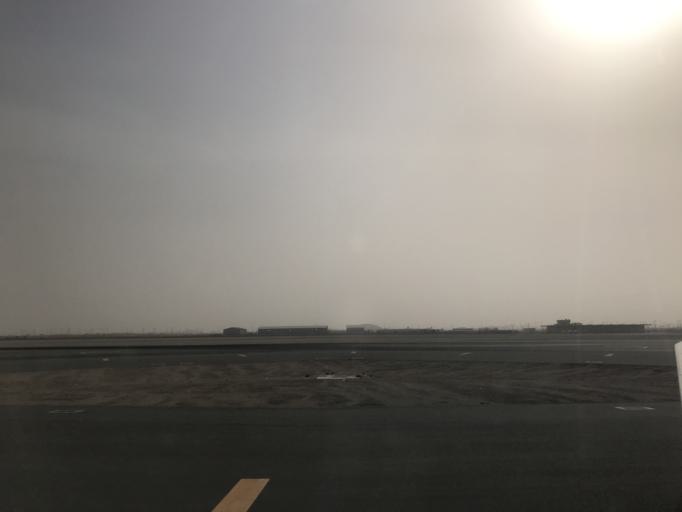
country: QA
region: Baladiyat ad Dawhah
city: Doha
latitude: 25.2734
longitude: 51.5995
